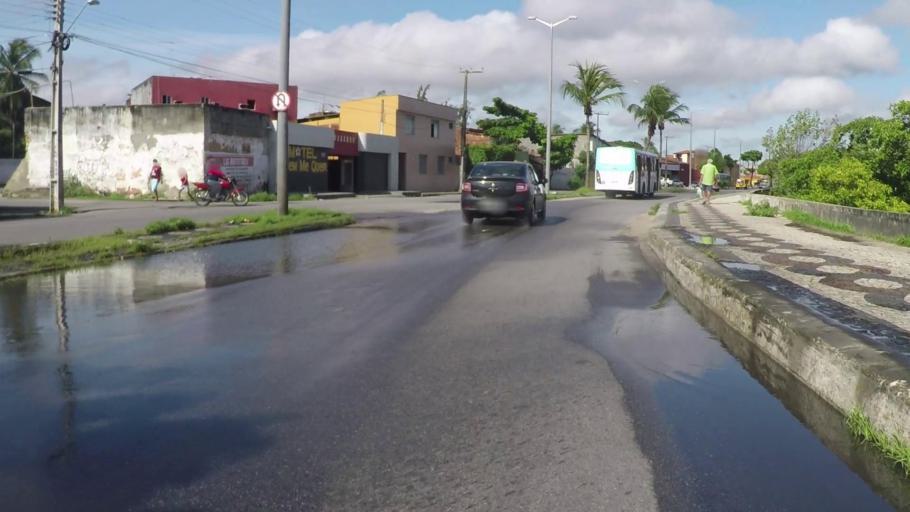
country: BR
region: Ceara
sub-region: Fortaleza
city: Fortaleza
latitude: -3.7016
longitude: -38.5898
